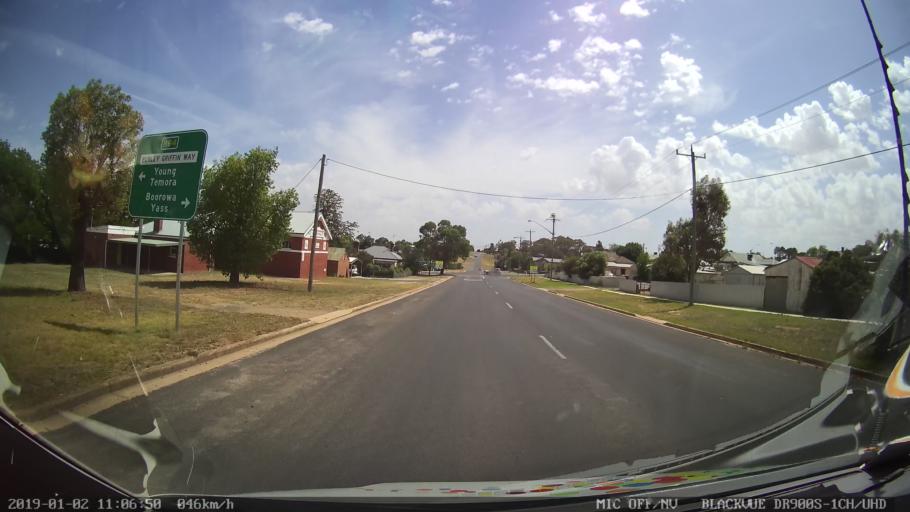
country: AU
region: New South Wales
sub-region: Young
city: Young
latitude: -34.5527
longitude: 148.3576
